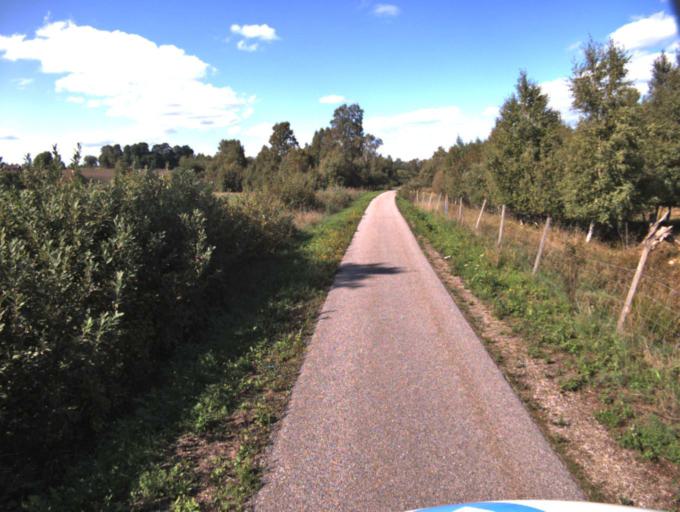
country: SE
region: Vaestra Goetaland
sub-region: Ulricehamns Kommun
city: Ulricehamn
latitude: 57.8397
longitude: 13.3047
